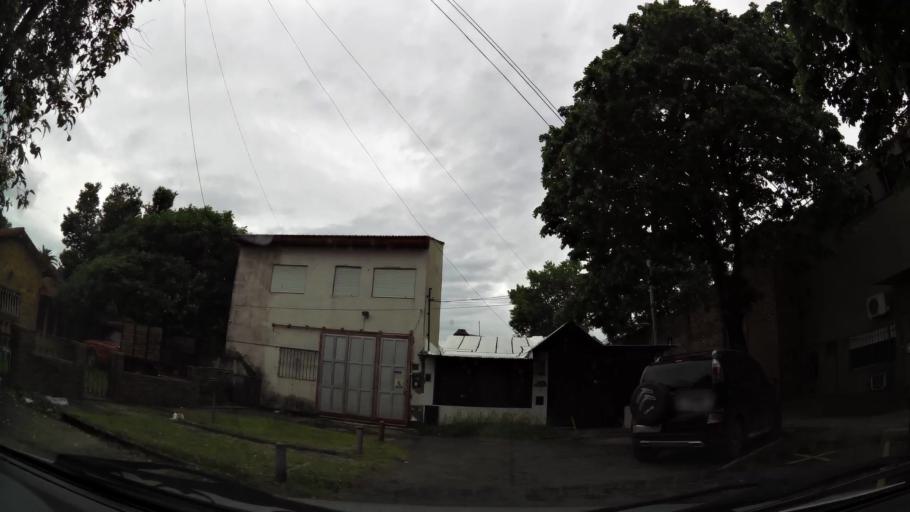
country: AR
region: Buenos Aires
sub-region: Partido de Lanus
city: Lanus
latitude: -34.7256
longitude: -58.3802
